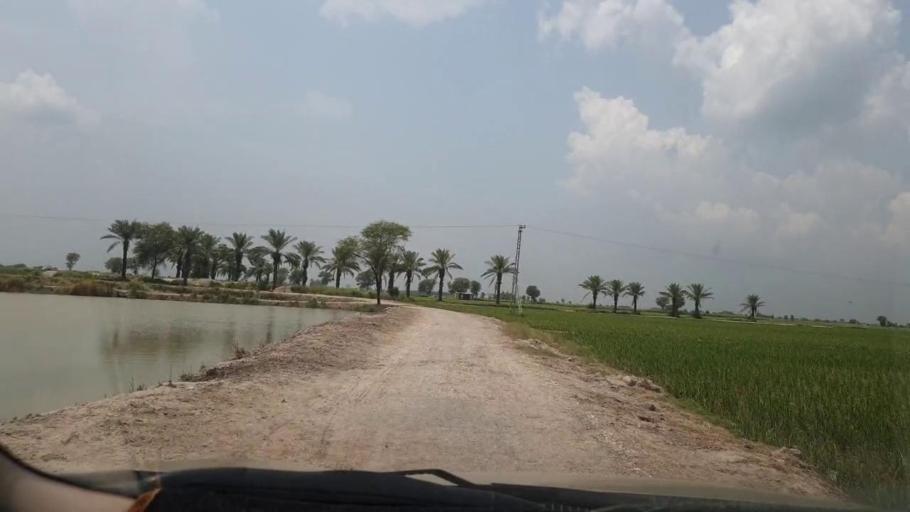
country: PK
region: Sindh
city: Larkana
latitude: 27.6151
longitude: 68.1512
